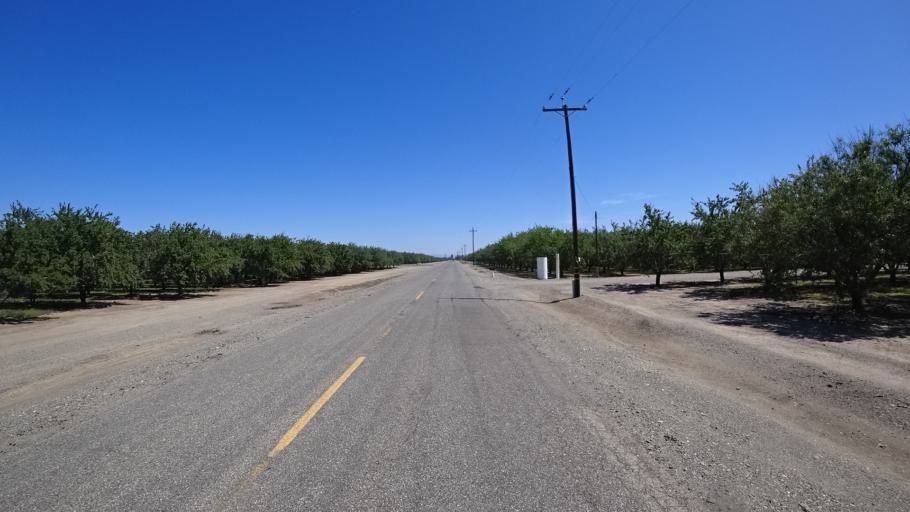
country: US
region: California
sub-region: Glenn County
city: Orland
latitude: 39.7251
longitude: -122.1341
